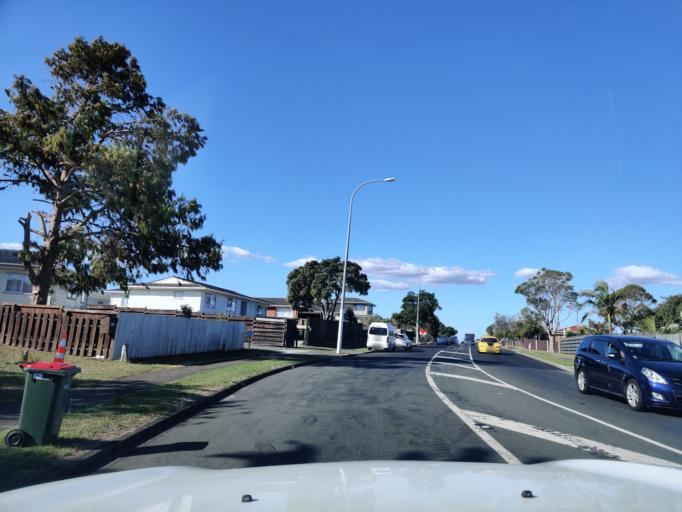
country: NZ
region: Auckland
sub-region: Auckland
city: Takanini
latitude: -37.0388
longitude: 174.8859
